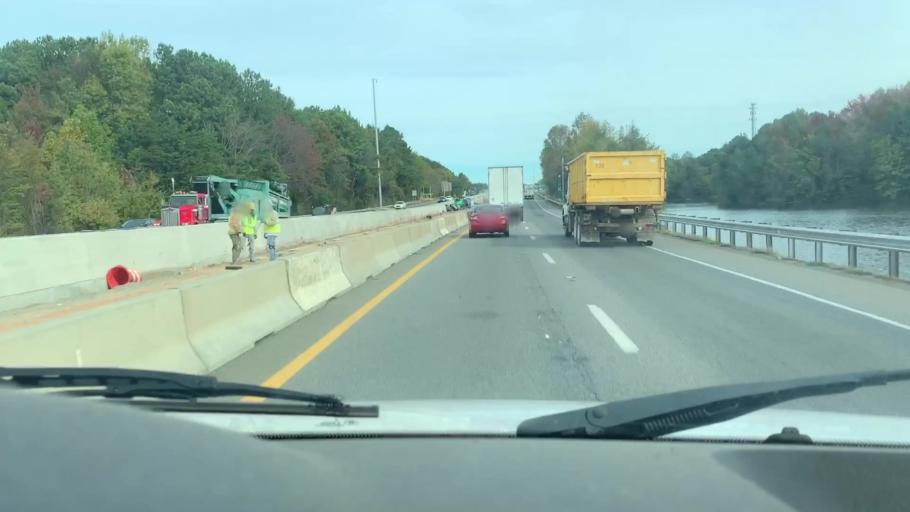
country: US
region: North Carolina
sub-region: Gaston County
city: Davidson
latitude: 35.5177
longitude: -80.8651
